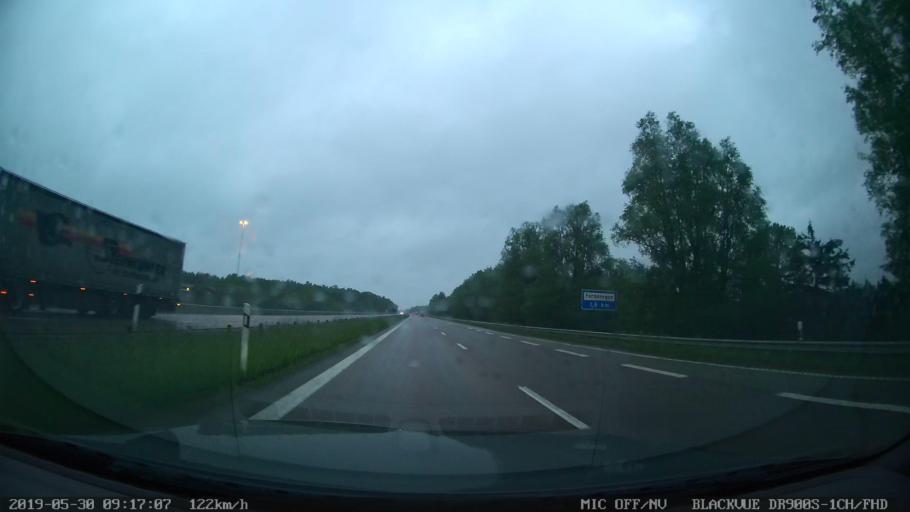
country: SE
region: Skane
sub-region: Helsingborg
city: Barslov
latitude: 56.0484
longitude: 12.7846
